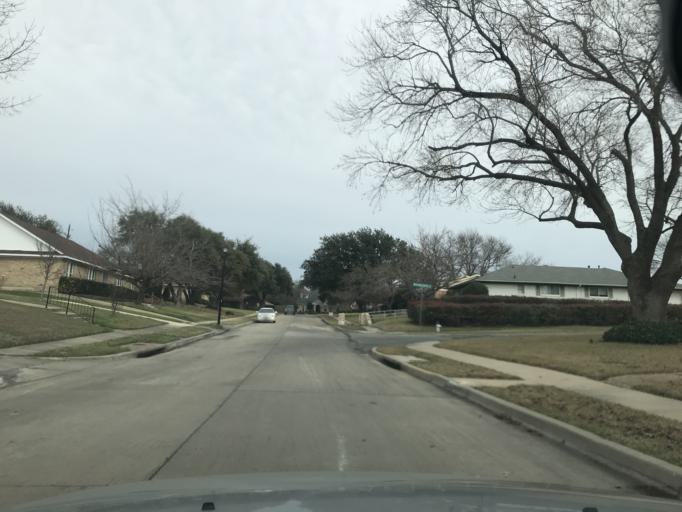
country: US
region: Texas
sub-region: Dallas County
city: Carrollton
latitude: 32.9829
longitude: -96.9017
